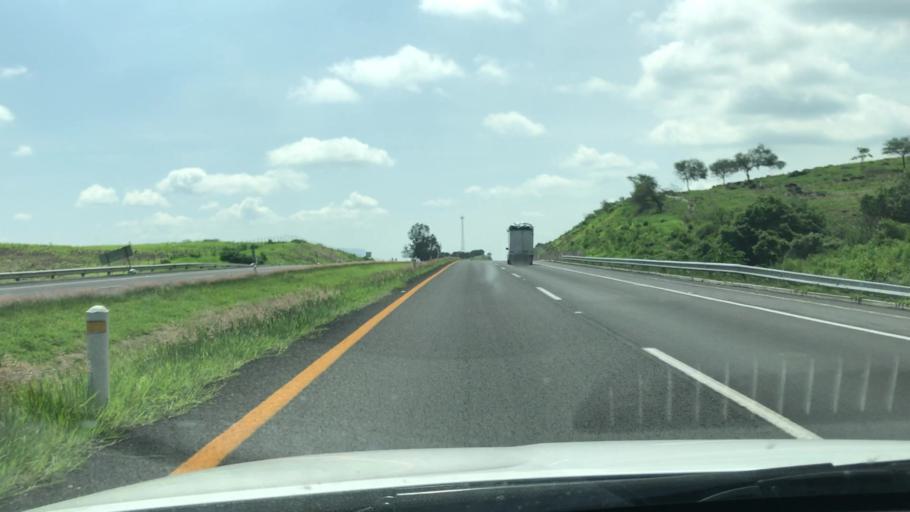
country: MX
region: Jalisco
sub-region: Poncitlan
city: Santa Cruz el Grande
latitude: 20.4407
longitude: -102.8180
